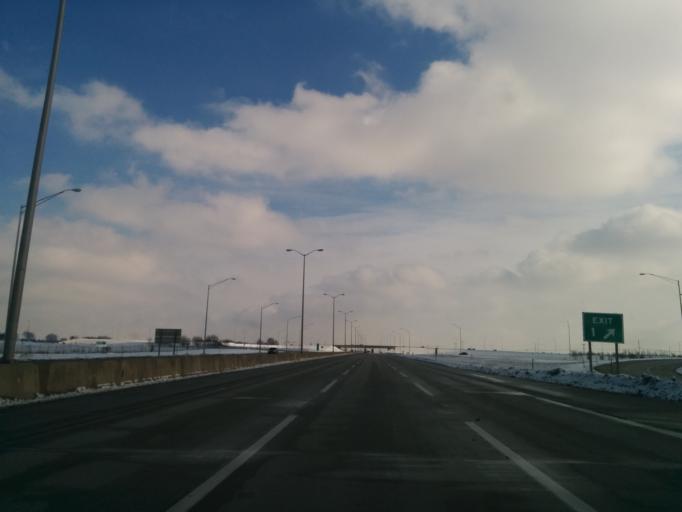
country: US
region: Illinois
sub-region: Will County
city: New Lenox
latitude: 41.5529
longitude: -87.9812
